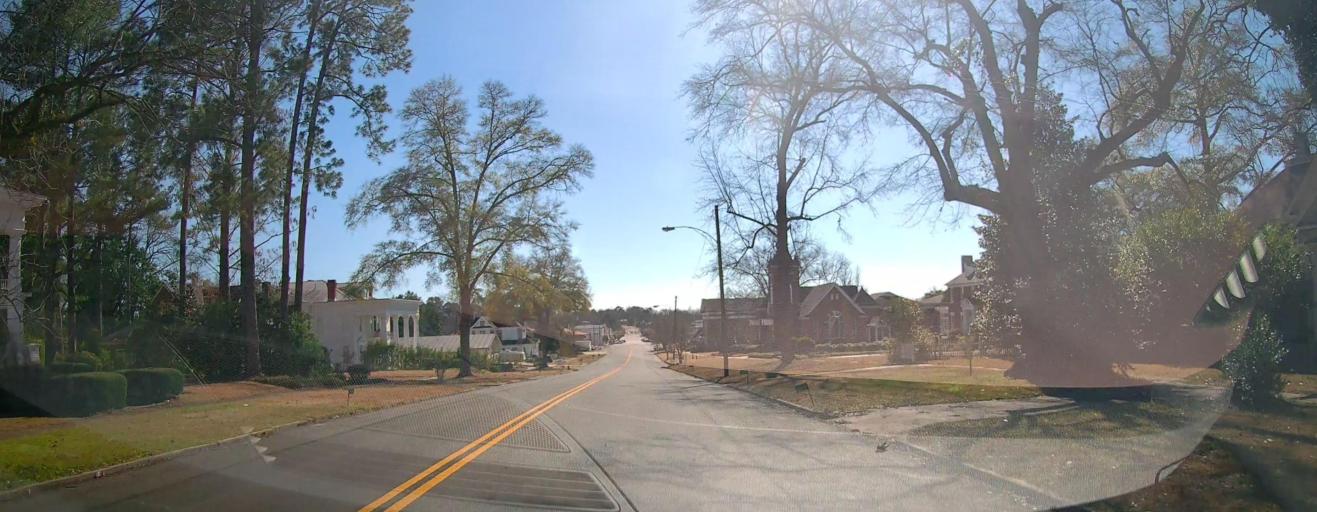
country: US
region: Georgia
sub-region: Macon County
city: Montezuma
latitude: 32.3038
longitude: -84.0285
